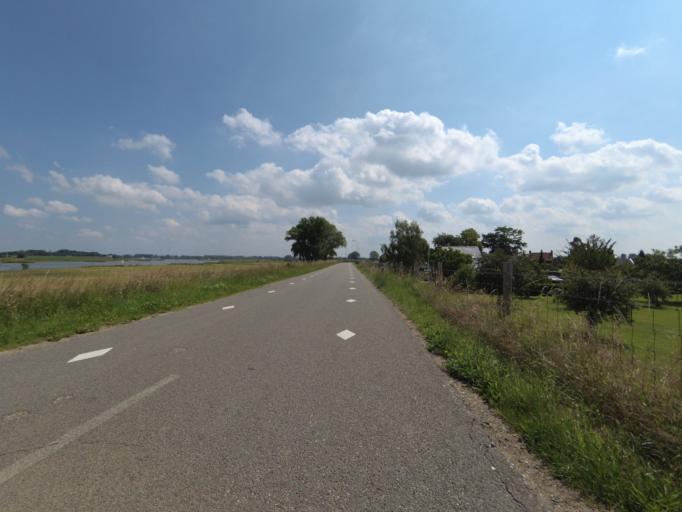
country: NL
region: Utrecht
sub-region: Gemeente Wijk bij Duurstede
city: Wijk bij Duurstede
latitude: 51.9533
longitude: 5.3253
